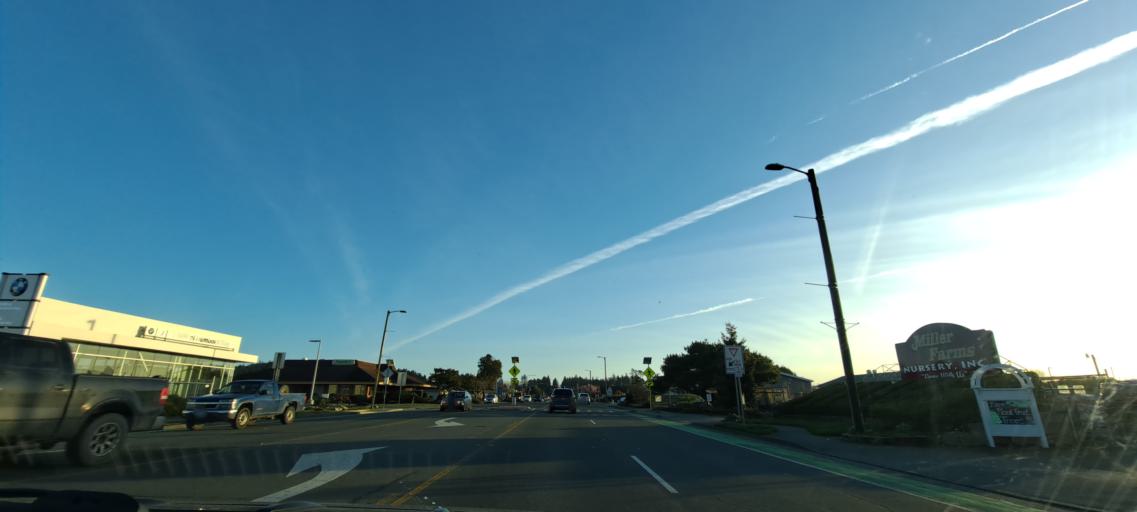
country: US
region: California
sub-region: Humboldt County
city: McKinleyville
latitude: 40.9380
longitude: -124.1010
